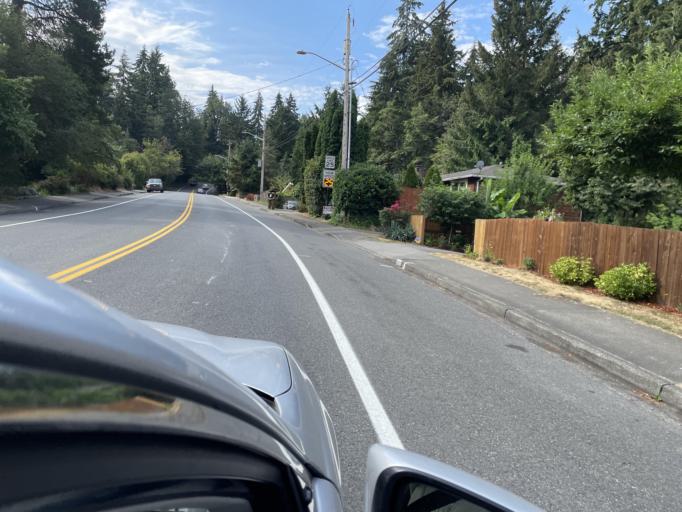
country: US
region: Washington
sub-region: King County
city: Eastgate
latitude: 47.5687
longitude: -122.1422
